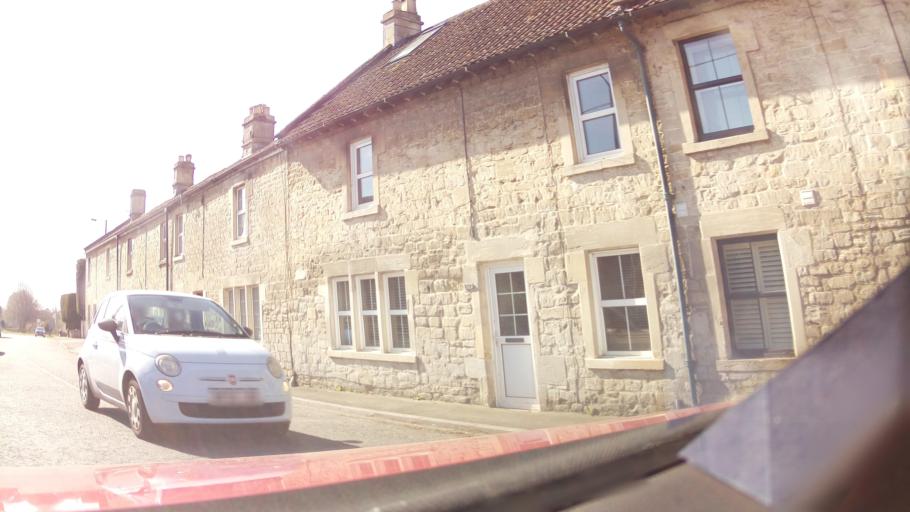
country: GB
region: England
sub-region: Wiltshire
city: Bradford-on-Avon
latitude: 51.3384
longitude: -2.2415
